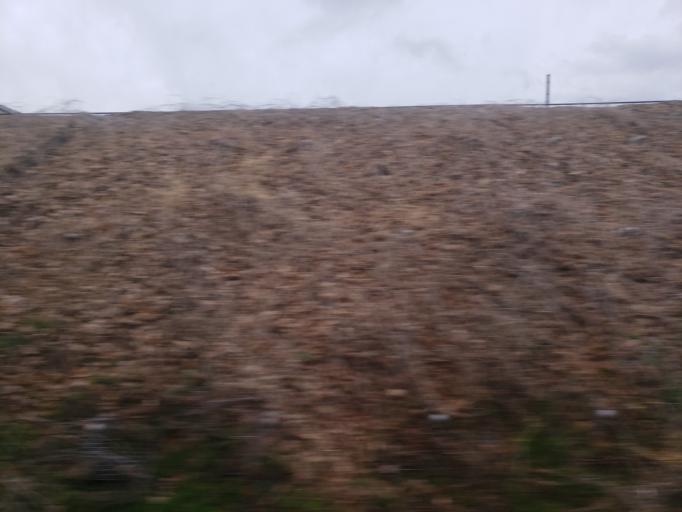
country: JP
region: Osaka
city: Osaka-shi
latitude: 34.7170
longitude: 135.4652
